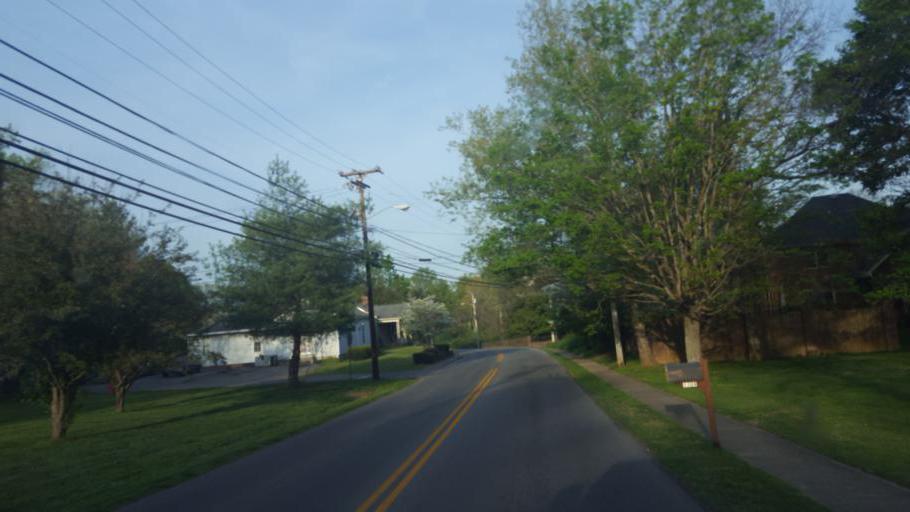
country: US
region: Kentucky
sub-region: Barren County
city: Glasgow
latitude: 36.9870
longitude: -85.9222
